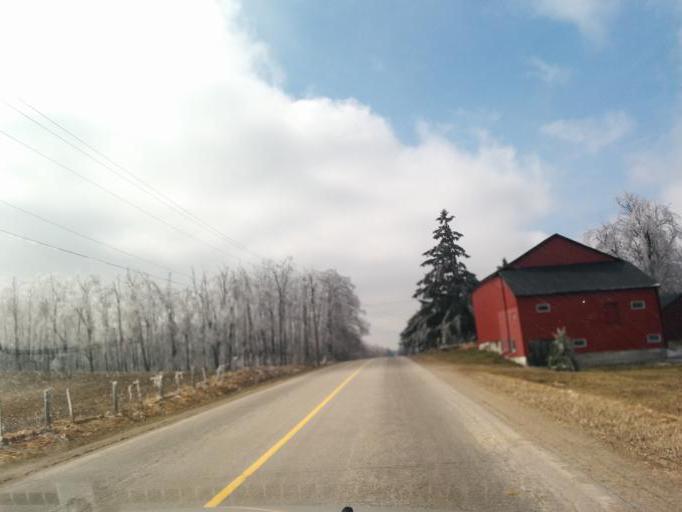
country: CA
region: Ontario
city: Waterloo
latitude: 43.6331
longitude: -80.5520
